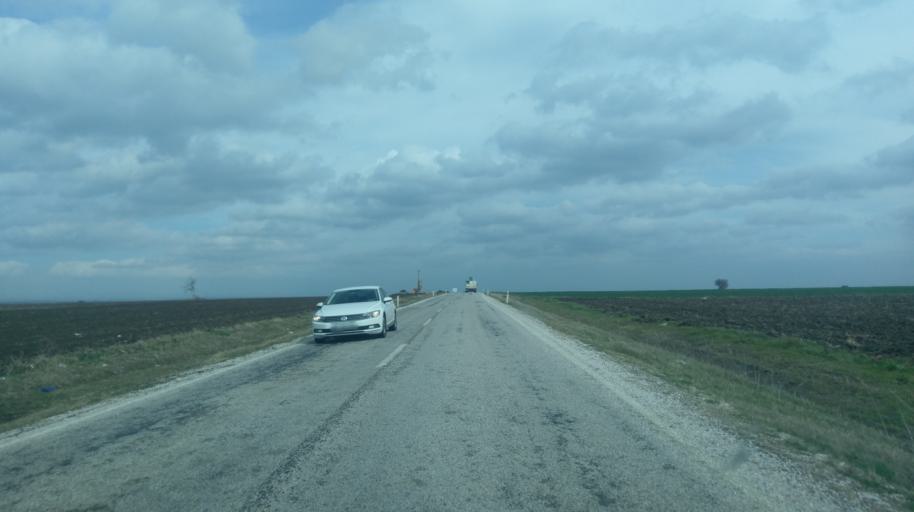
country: TR
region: Edirne
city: Haskoy
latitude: 41.6523
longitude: 26.8971
